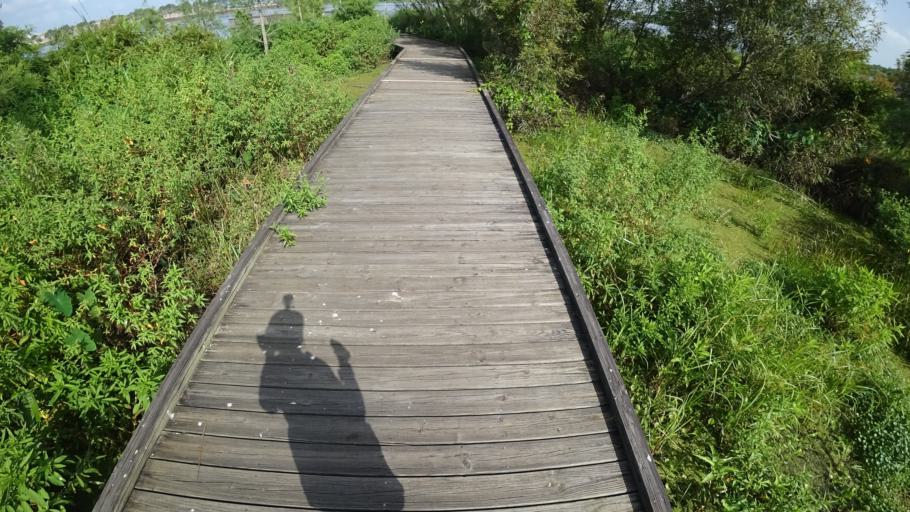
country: US
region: Florida
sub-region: Sarasota County
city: Desoto Lakes
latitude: 27.4325
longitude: -82.4830
